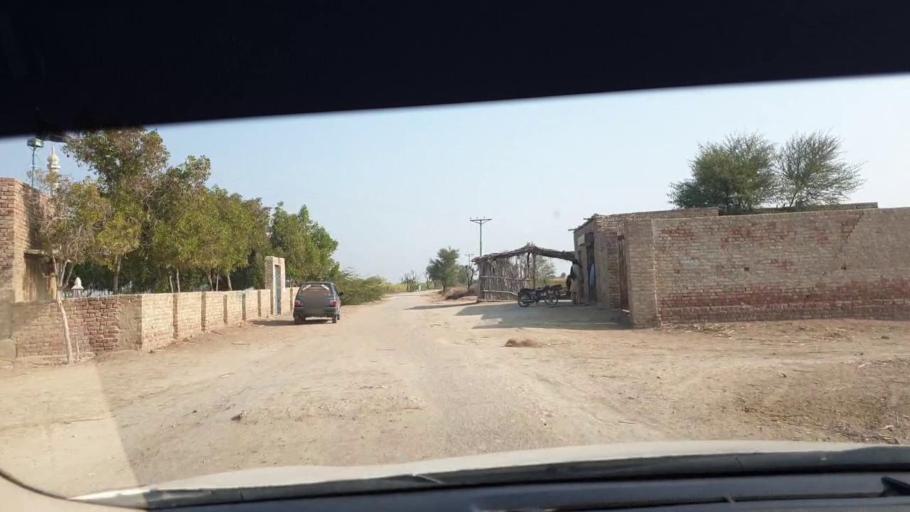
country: PK
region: Sindh
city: Berani
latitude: 25.8211
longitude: 68.7703
